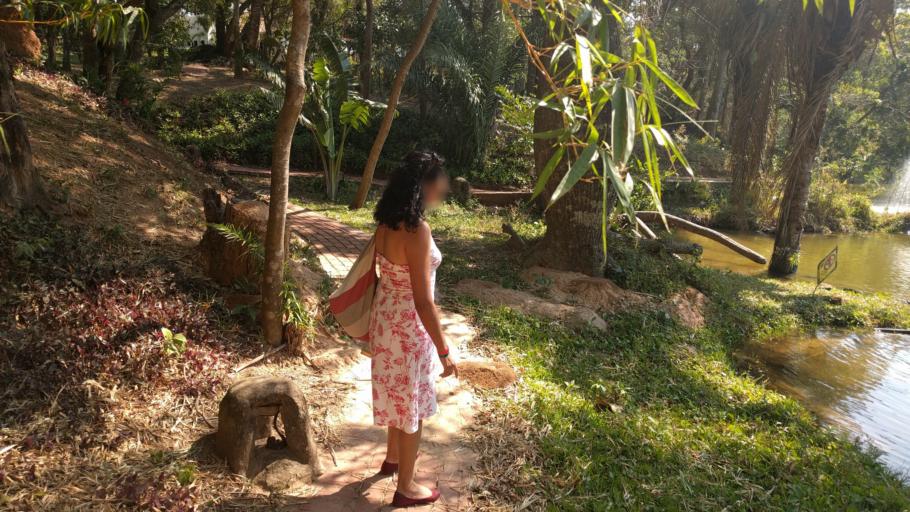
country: BO
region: Santa Cruz
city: Santa Cruz de la Sierra
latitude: -17.7694
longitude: -63.2477
